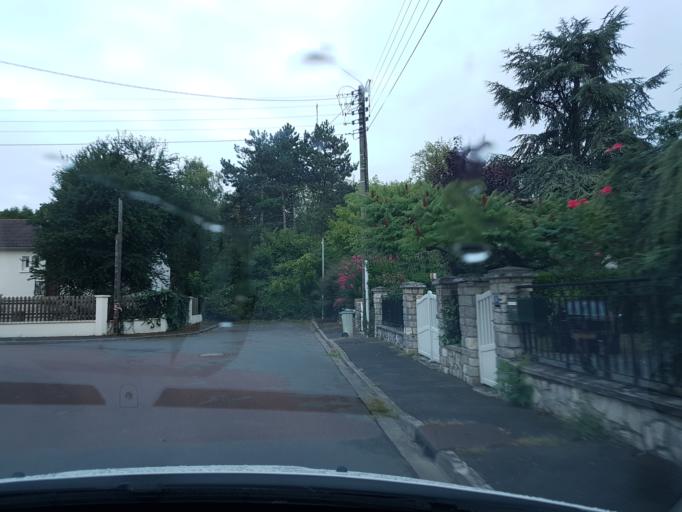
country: FR
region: Centre
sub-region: Departement d'Indre-et-Loire
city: Saint-Avertin
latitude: 47.3681
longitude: 0.7462
